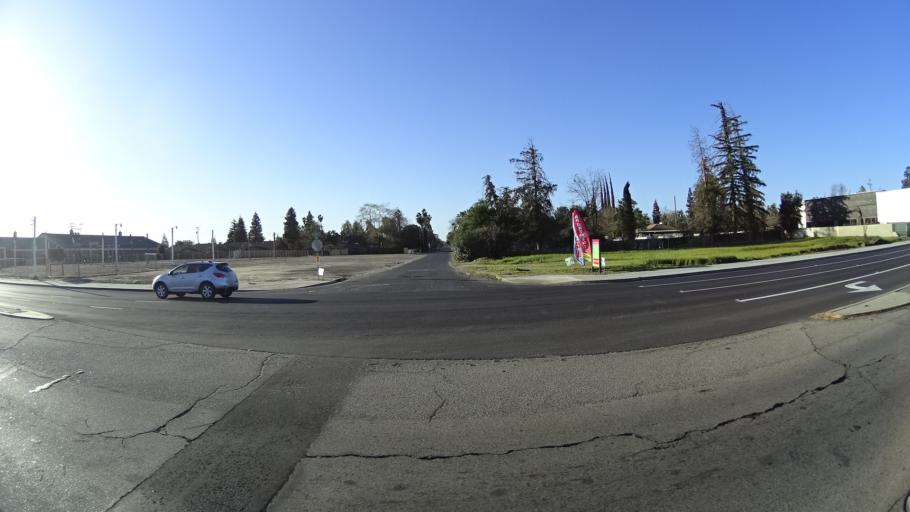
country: US
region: California
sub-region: Fresno County
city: Fresno
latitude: 36.8086
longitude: -119.7927
